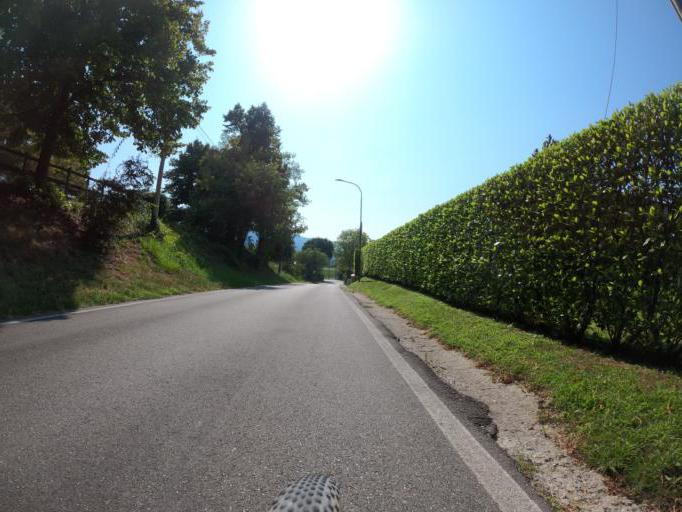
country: IT
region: Veneto
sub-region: Provincia di Verona
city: Caprino Veronese
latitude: 45.5849
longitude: 10.7926
